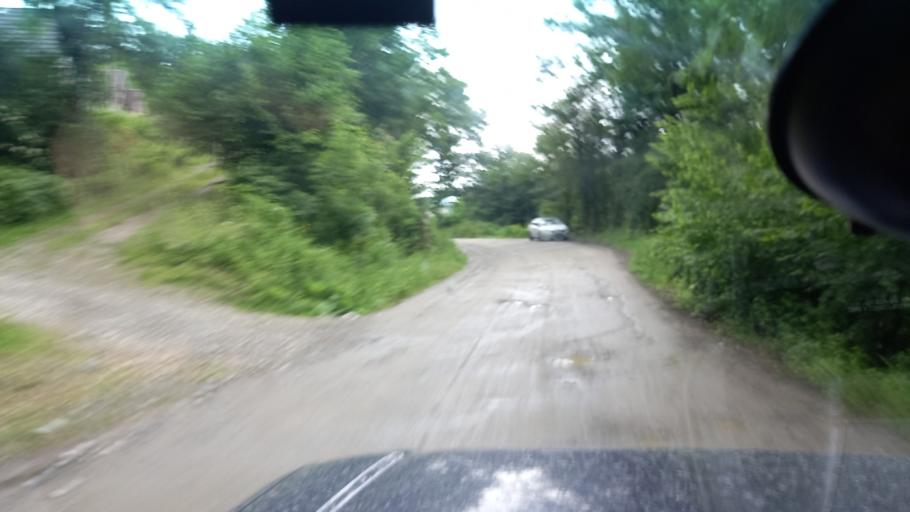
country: RU
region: Krasnodarskiy
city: Psebay
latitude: 44.0407
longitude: 40.7563
